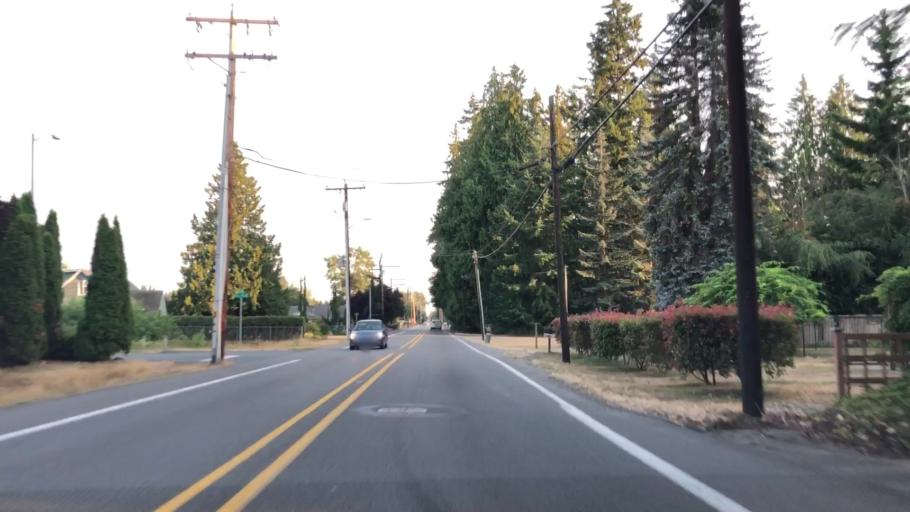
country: US
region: Washington
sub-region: Snohomish County
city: Marysville
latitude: 48.0988
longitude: -122.1623
